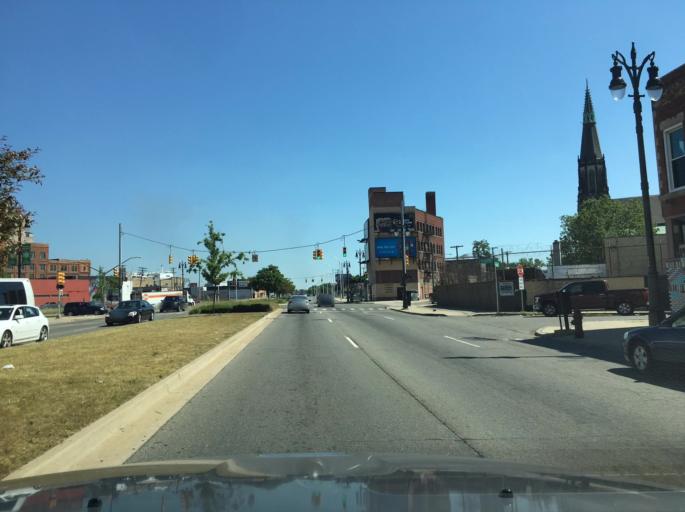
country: US
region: Michigan
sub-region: Wayne County
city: Detroit
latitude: 42.3446
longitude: -83.0378
